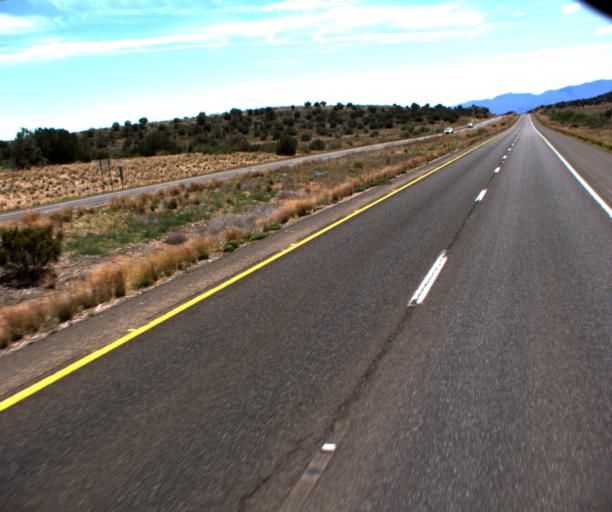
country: US
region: Arizona
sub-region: Yavapai County
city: Cornville
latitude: 34.8123
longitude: -111.9063
